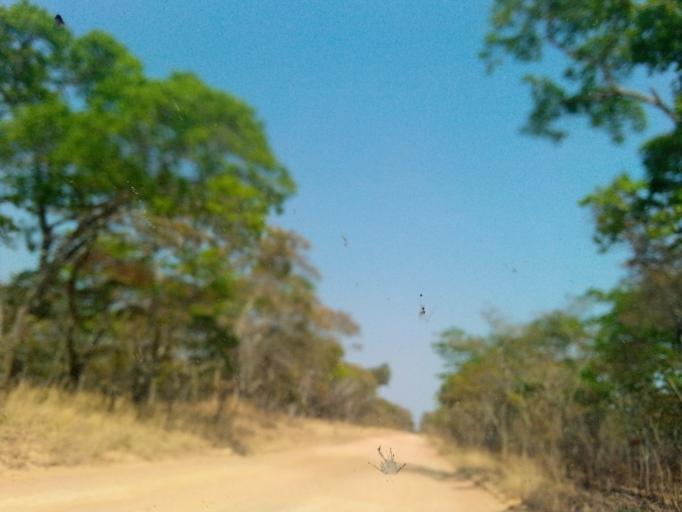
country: ZM
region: Northern
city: Mpika
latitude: -12.2419
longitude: 30.8516
